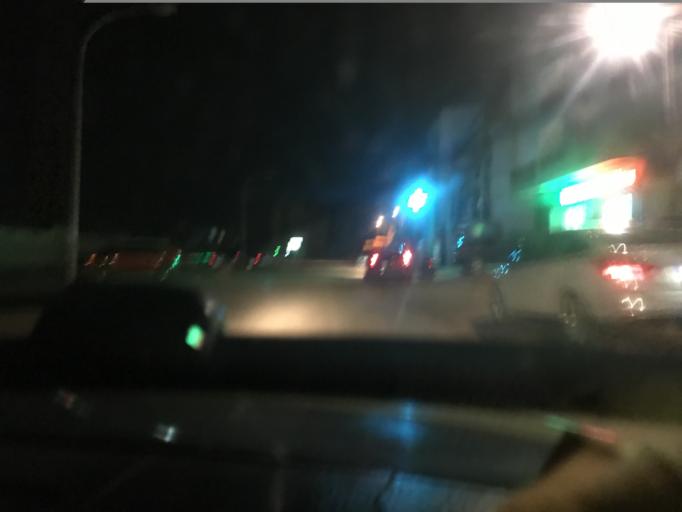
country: SN
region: Dakar
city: Grand Dakar
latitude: 14.7487
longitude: -17.4527
